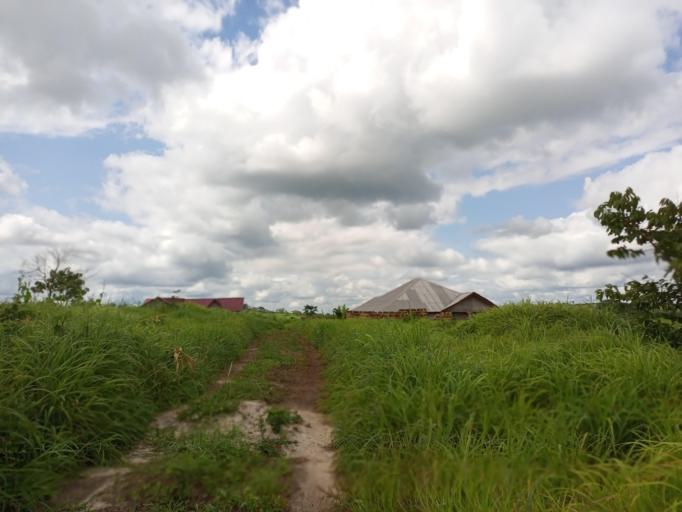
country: SL
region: Northern Province
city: Kamakwie
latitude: 9.5069
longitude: -12.2305
